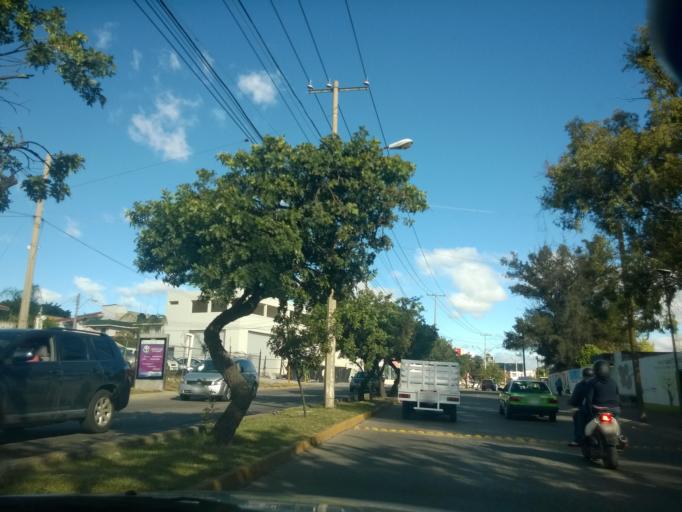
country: MX
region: Guanajuato
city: Leon
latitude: 21.1172
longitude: -101.7028
